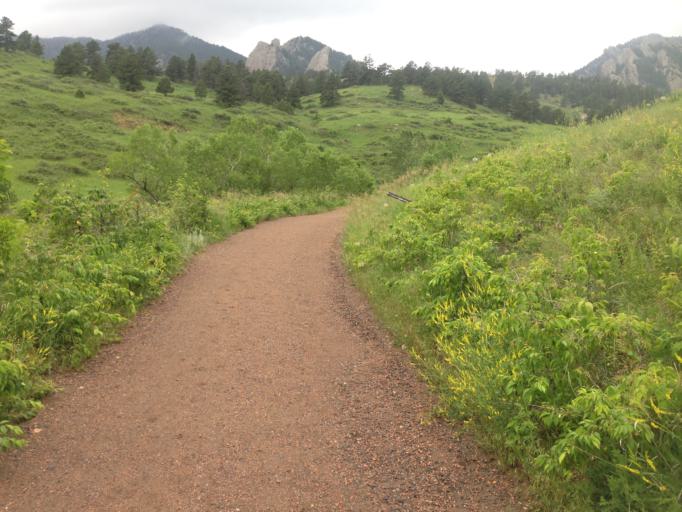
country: US
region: Colorado
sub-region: Boulder County
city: Boulder
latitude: 39.9731
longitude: -105.2723
